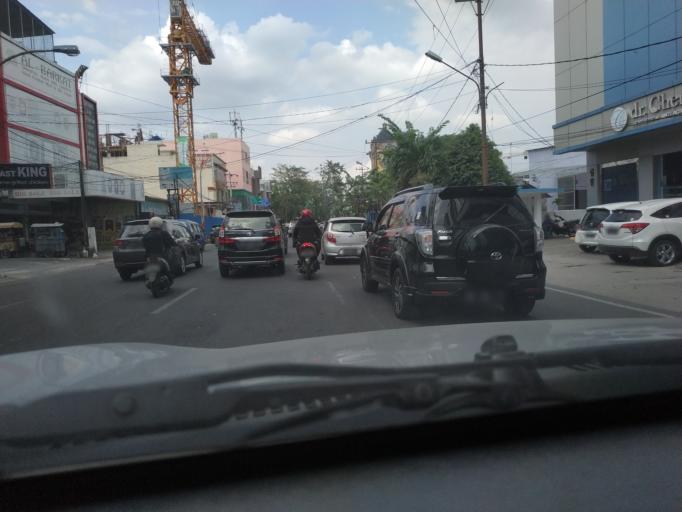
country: ID
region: North Sumatra
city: Medan
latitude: 3.5855
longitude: 98.6670
